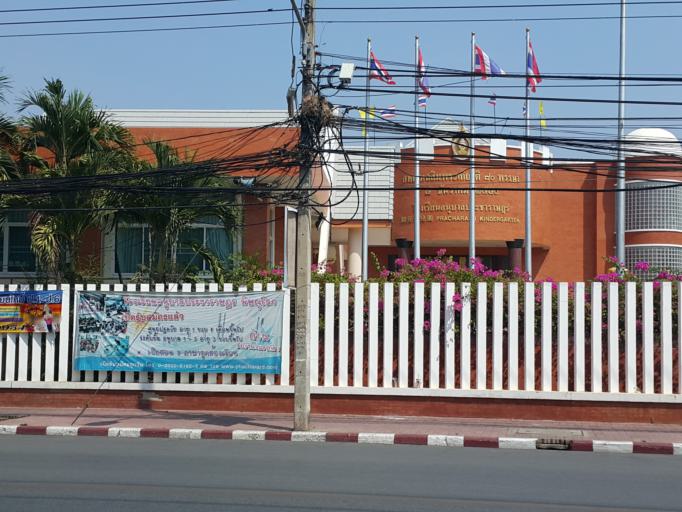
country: TH
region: Phitsanulok
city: Phitsanulok
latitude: 16.8120
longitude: 100.2613
